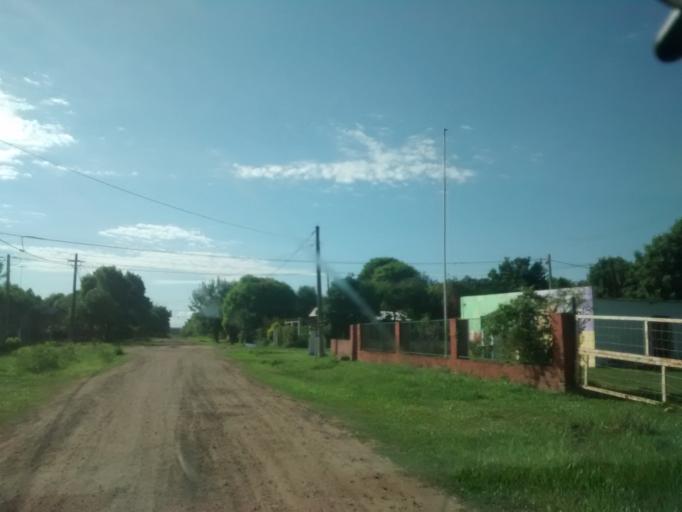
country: AR
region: Chaco
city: Puerto Tirol
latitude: -27.3752
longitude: -59.0968
